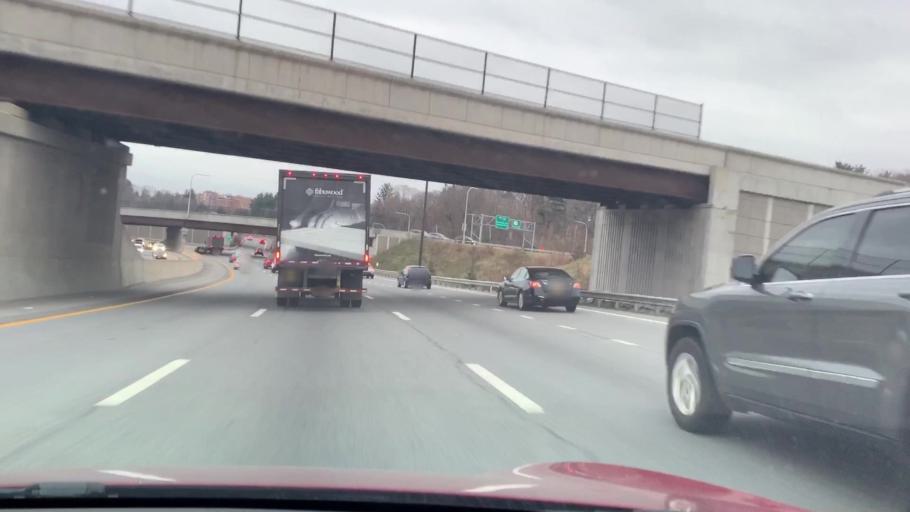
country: US
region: New York
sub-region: Westchester County
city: White Plains
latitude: 41.0337
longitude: -73.7538
